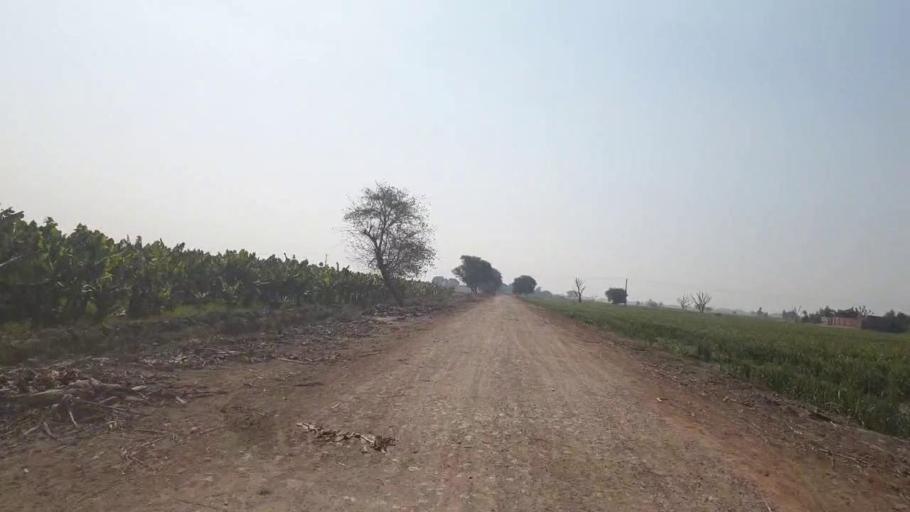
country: PK
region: Sindh
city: Tando Allahyar
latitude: 25.6130
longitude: 68.7362
